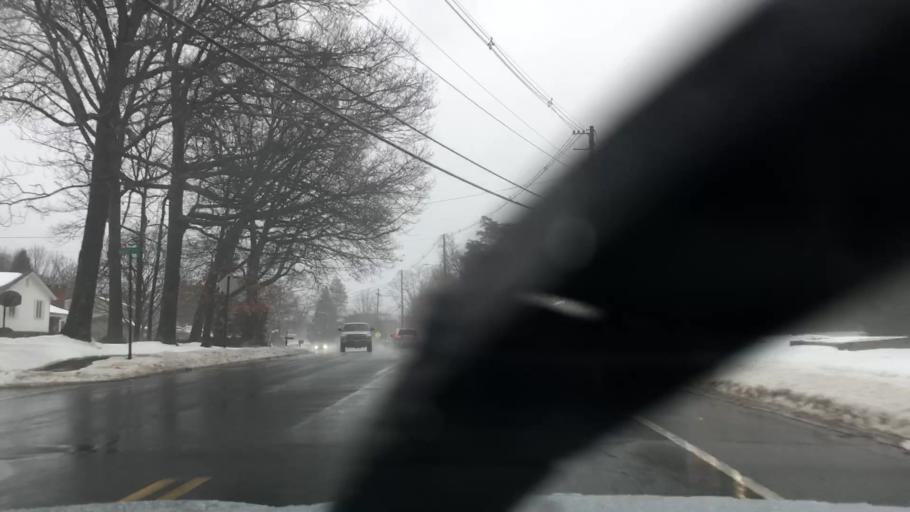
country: US
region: Massachusetts
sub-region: Hampden County
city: Ludlow
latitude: 42.1756
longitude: -72.5290
